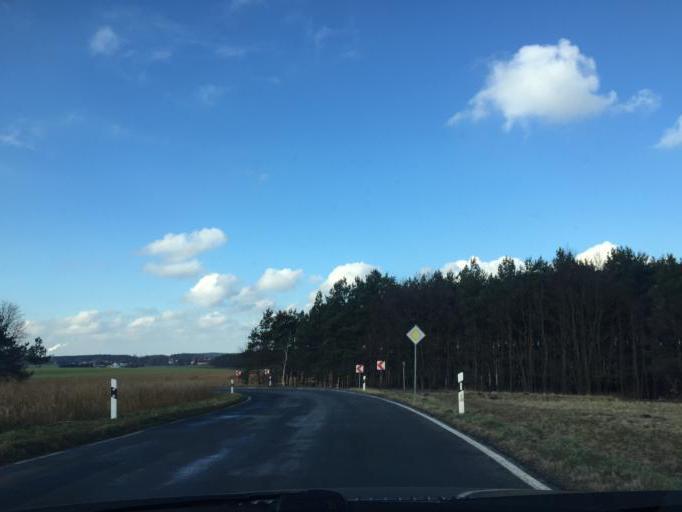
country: DE
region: Saxony
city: Thiendorf
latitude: 51.2717
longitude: 13.7629
